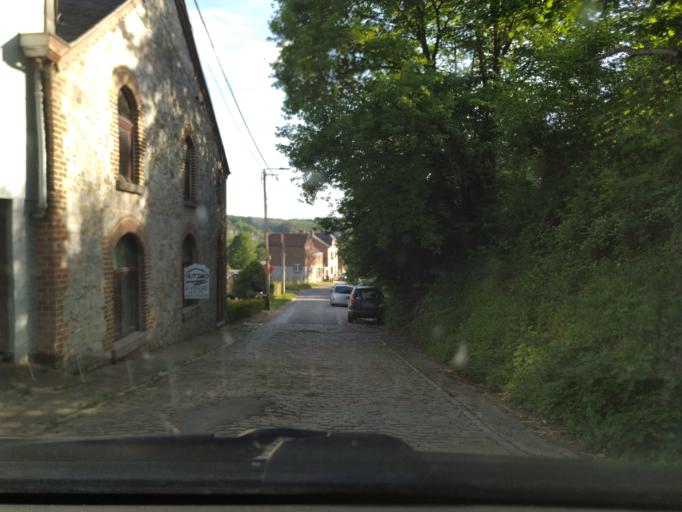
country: BE
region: Wallonia
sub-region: Province de Namur
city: Namur
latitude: 50.4762
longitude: 4.9310
